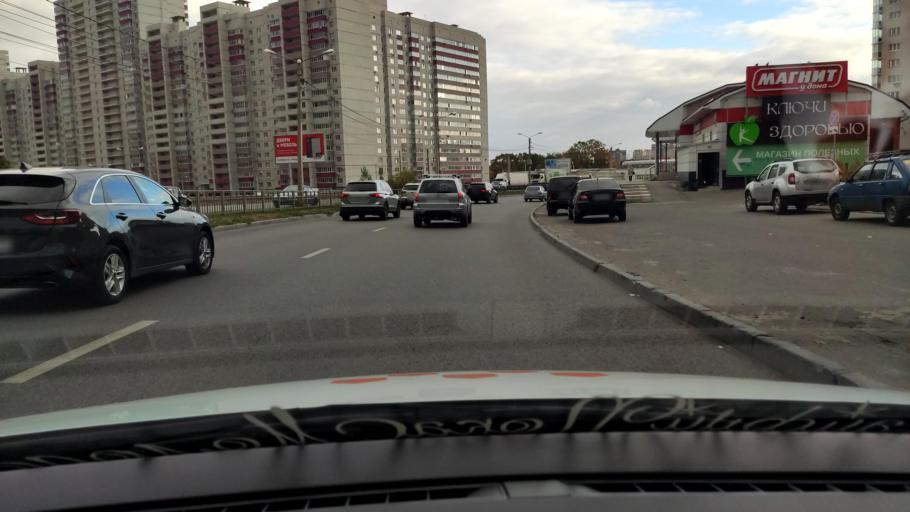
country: RU
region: Voronezj
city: Voronezh
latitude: 51.7131
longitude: 39.1934
